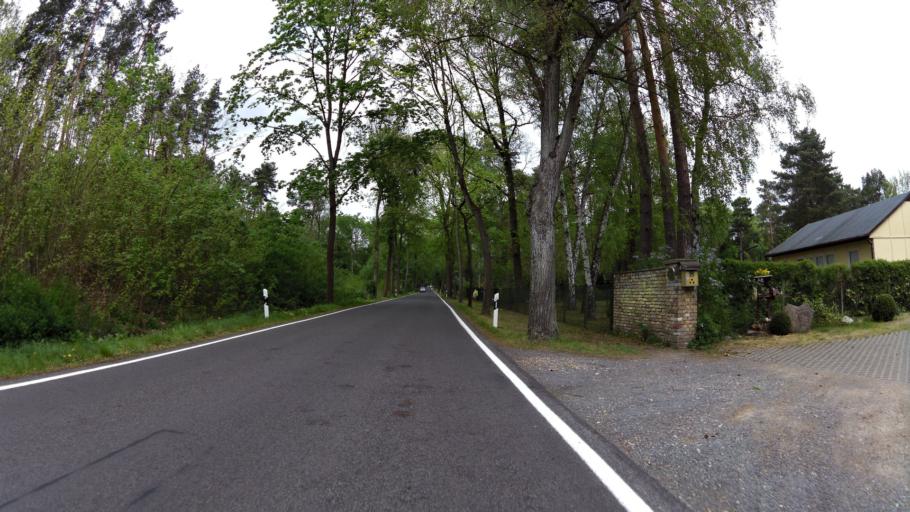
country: DE
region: Brandenburg
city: Schwerin
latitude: 52.1968
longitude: 13.5772
